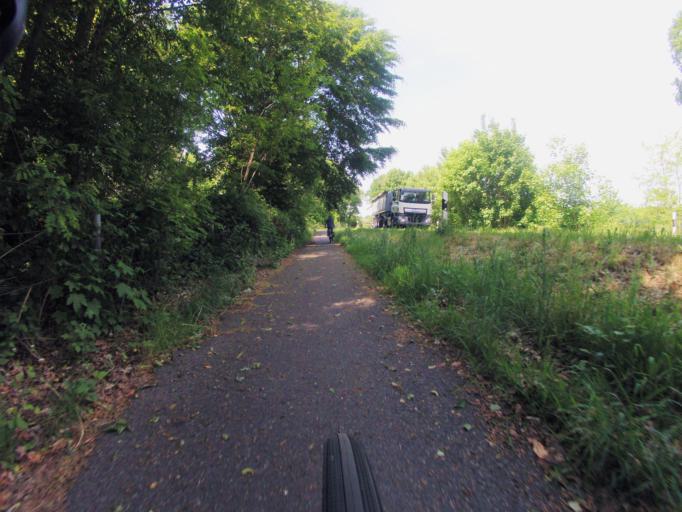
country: DE
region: North Rhine-Westphalia
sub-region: Regierungsbezirk Munster
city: Horstel
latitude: 52.3044
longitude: 7.6353
